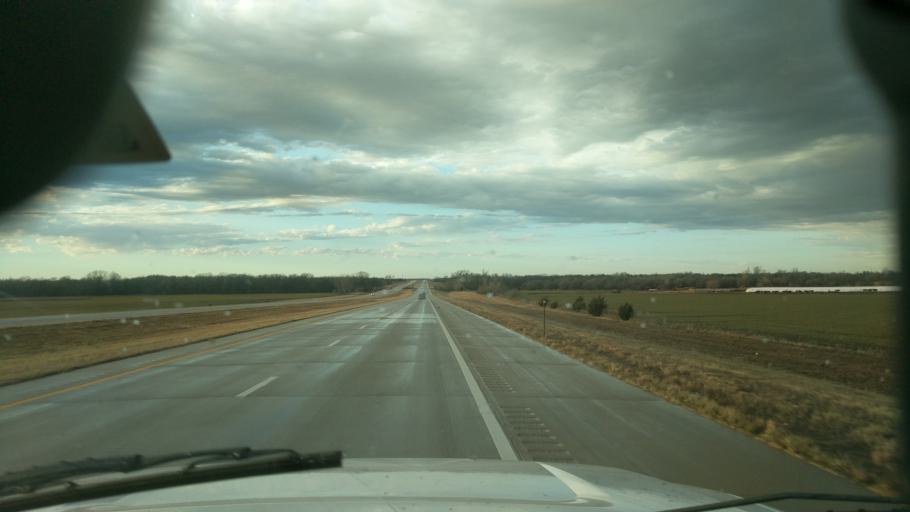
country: US
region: Kansas
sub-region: Harvey County
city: North Newton
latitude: 38.1031
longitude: -97.3731
